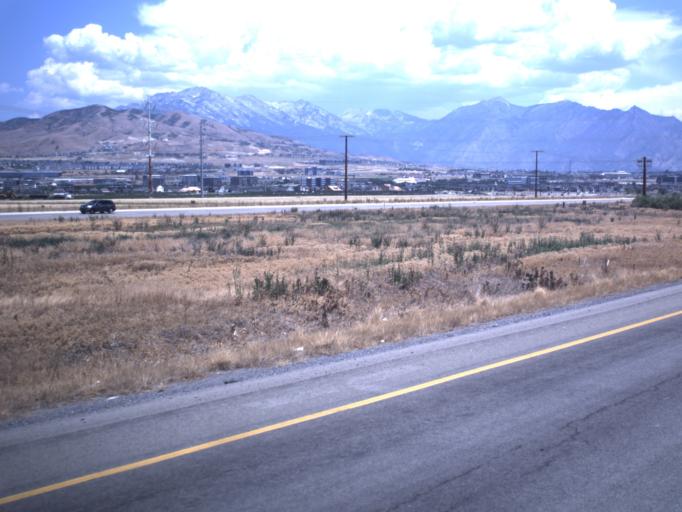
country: US
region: Utah
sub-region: Utah County
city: Saratoga Springs
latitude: 40.4126
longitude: -111.9138
